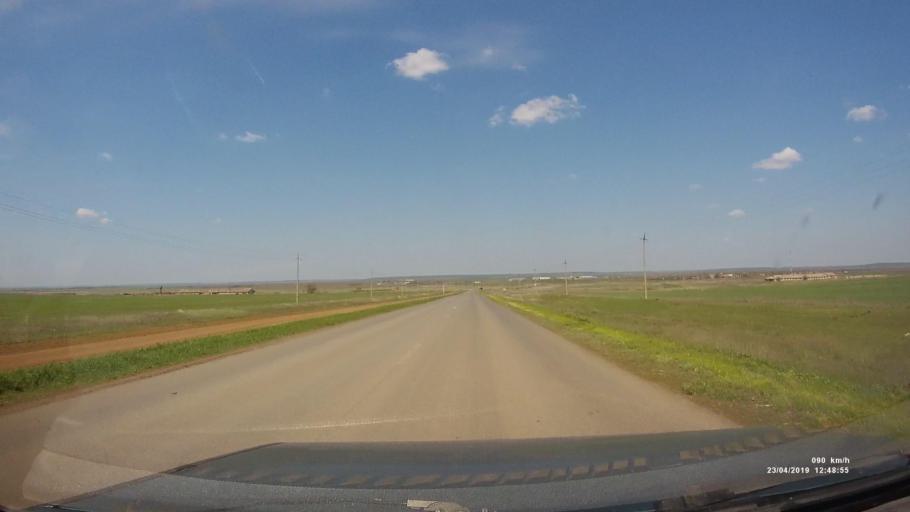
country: RU
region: Kalmykiya
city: Yashalta
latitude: 46.5306
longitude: 42.6389
